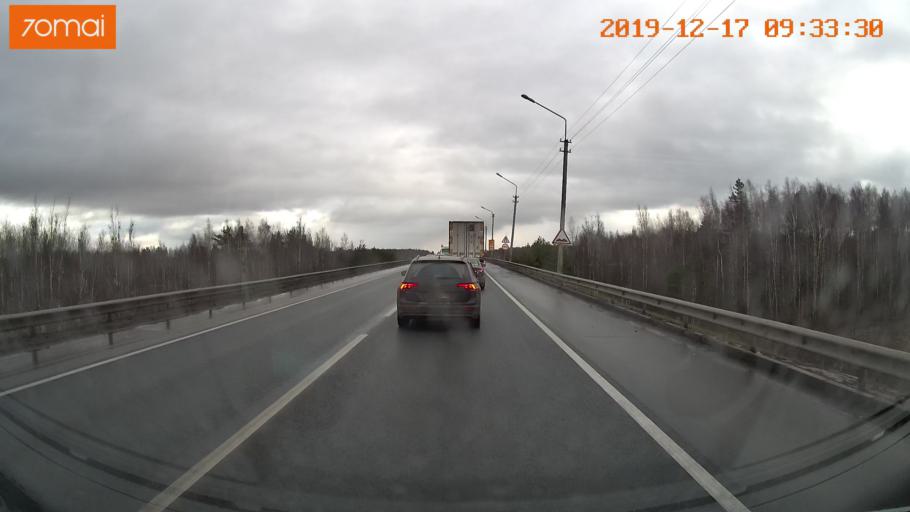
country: RU
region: Vladimir
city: Vorsha
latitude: 56.0770
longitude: 40.2091
